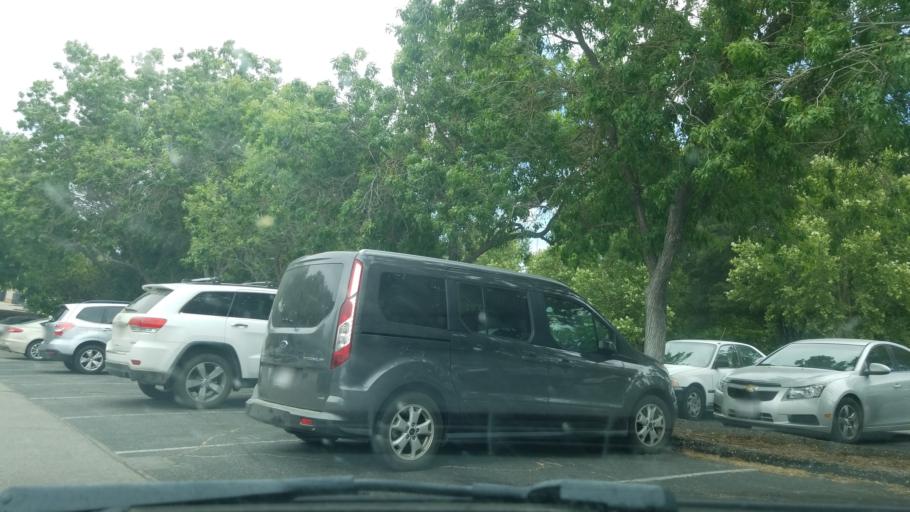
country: US
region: California
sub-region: San Luis Obispo County
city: Atascadero
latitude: 35.4673
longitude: -120.6699
